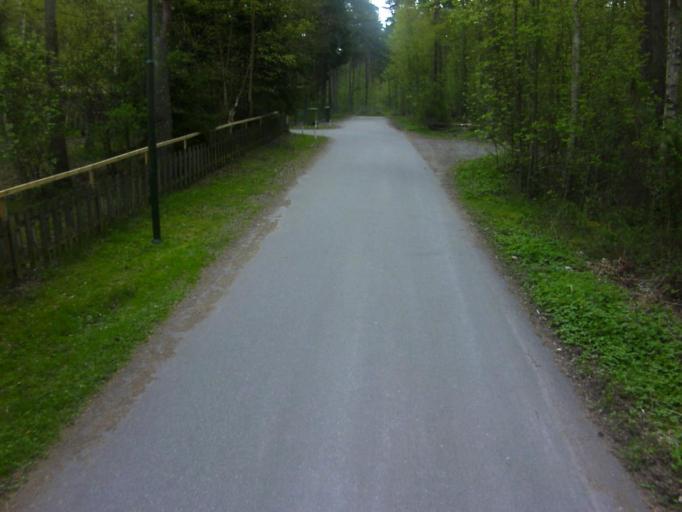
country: SE
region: Skane
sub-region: Kavlinge Kommun
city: Hofterup
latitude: 55.7568
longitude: 12.9831
